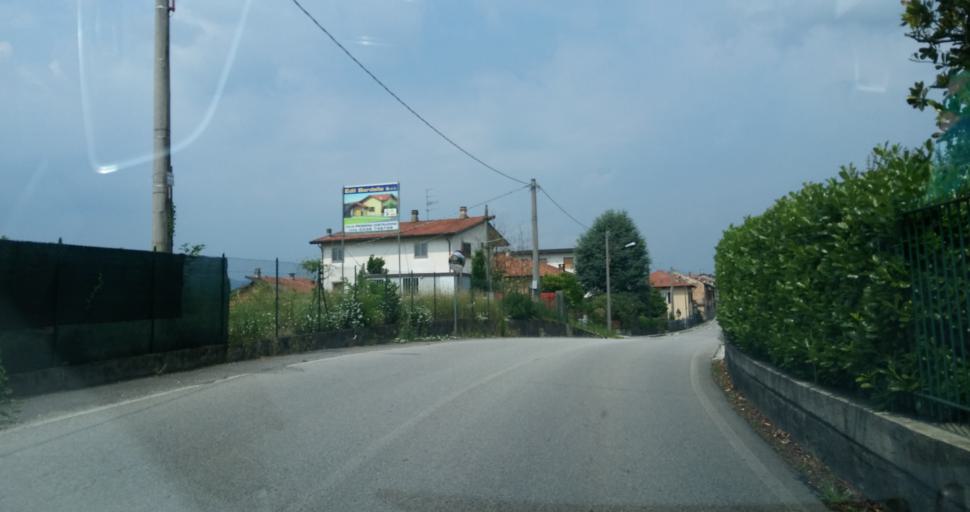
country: IT
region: Lombardy
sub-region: Provincia di Varese
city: Bardello
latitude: 45.8331
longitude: 8.7018
